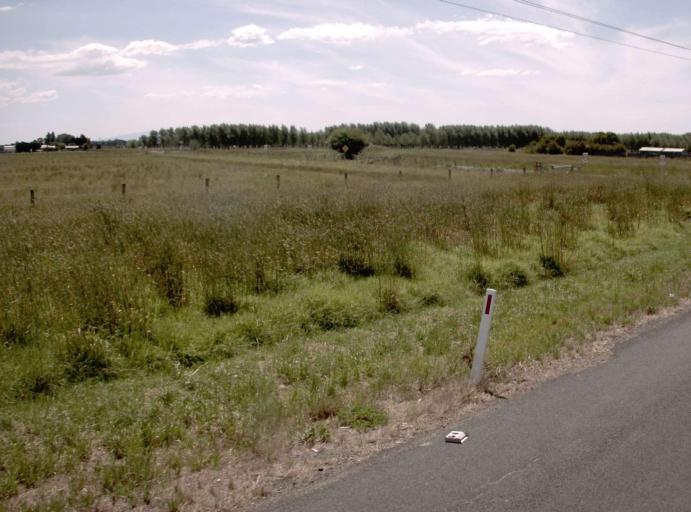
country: AU
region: Victoria
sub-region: Wellington
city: Sale
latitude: -38.0582
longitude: 147.0695
